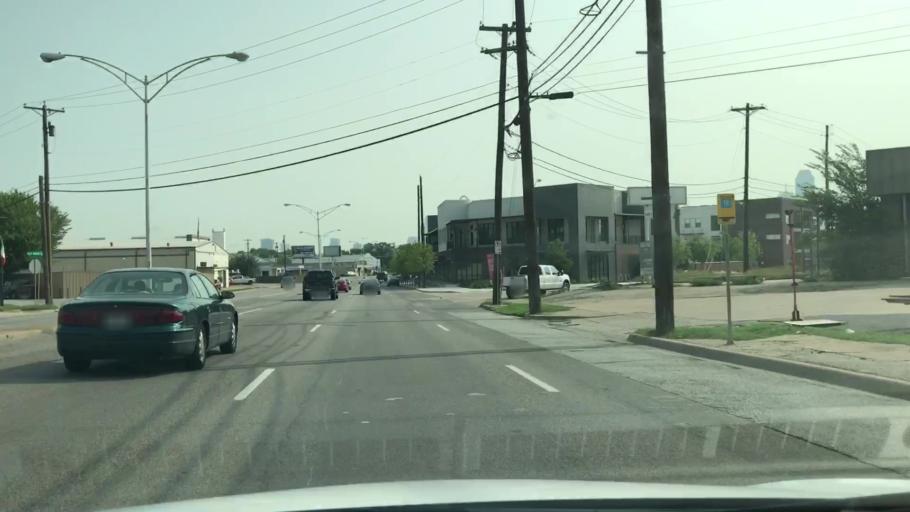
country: US
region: Texas
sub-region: Dallas County
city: Dallas
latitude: 32.7706
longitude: -96.8349
